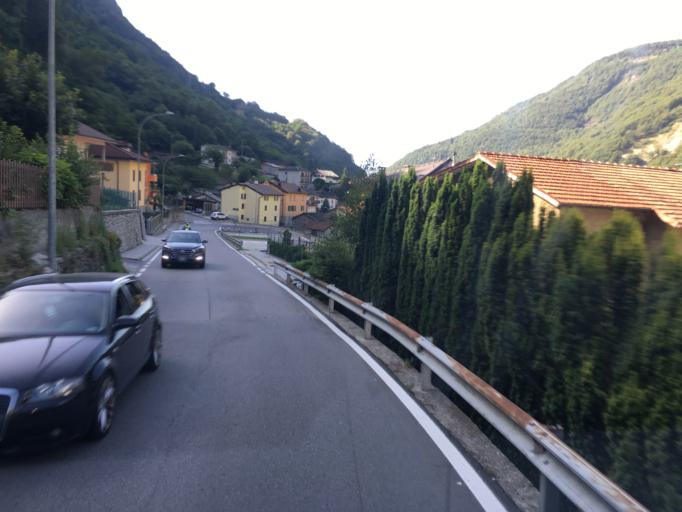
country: IT
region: Lombardy
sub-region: Provincia di Sondrio
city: San Giacomo Filippo
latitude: 46.3389
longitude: 9.3704
